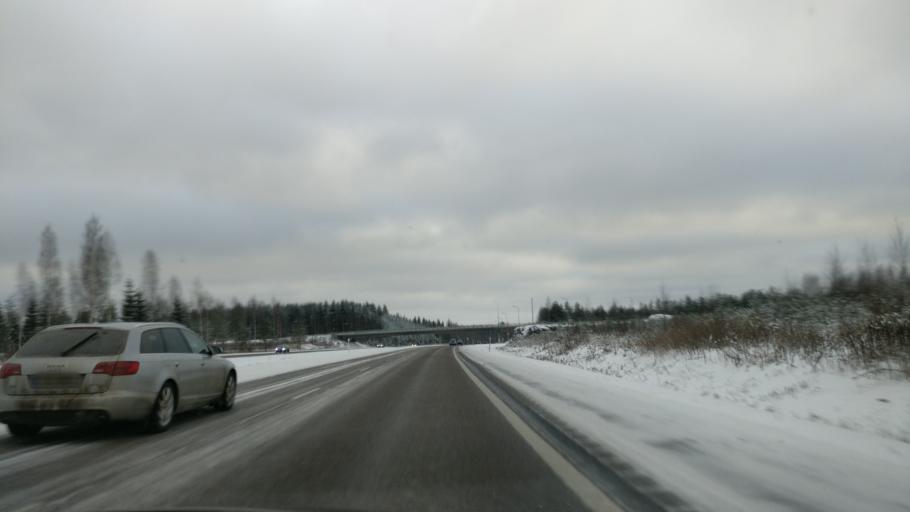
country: FI
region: Paijanne Tavastia
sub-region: Lahti
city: Nastola
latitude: 61.0468
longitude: 25.8528
